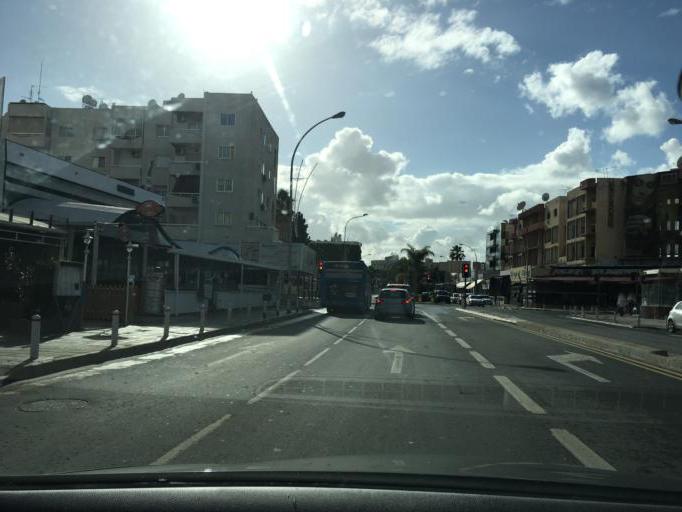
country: CY
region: Limassol
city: Mouttagiaka
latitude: 34.6977
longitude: 33.0935
